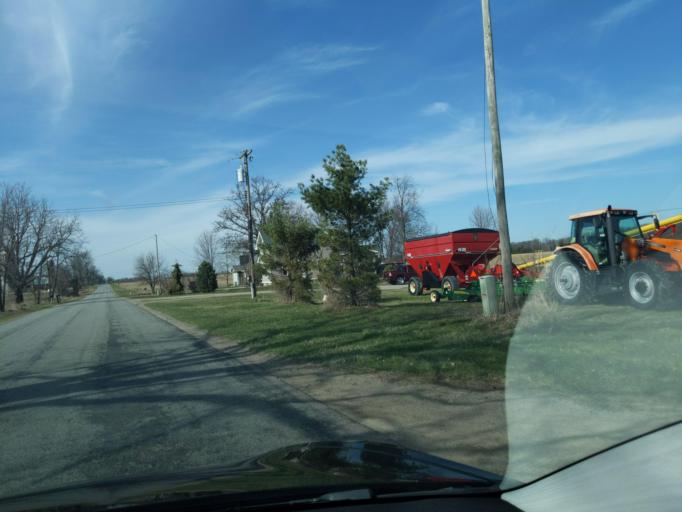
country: US
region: Michigan
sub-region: Ingham County
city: Williamston
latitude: 42.6232
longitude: -84.3096
